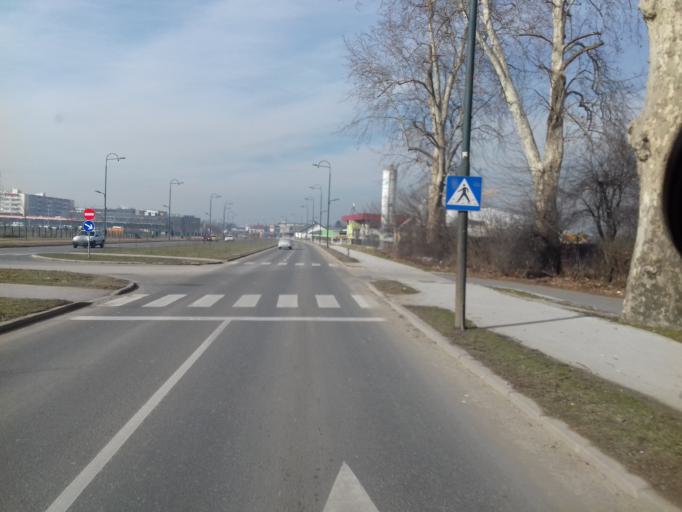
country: BA
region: Federation of Bosnia and Herzegovina
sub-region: Kanton Sarajevo
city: Sarajevo
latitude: 43.8269
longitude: 18.3165
